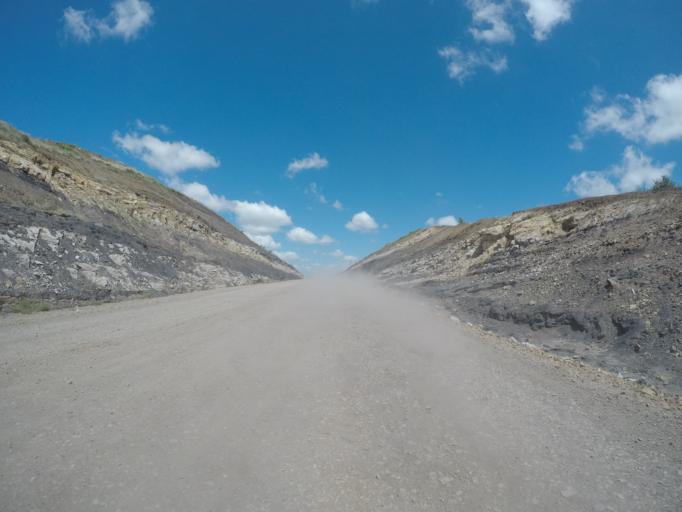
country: ZA
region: KwaZulu-Natal
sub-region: uThungulu District Municipality
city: Empangeni
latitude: -28.6271
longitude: 31.7586
